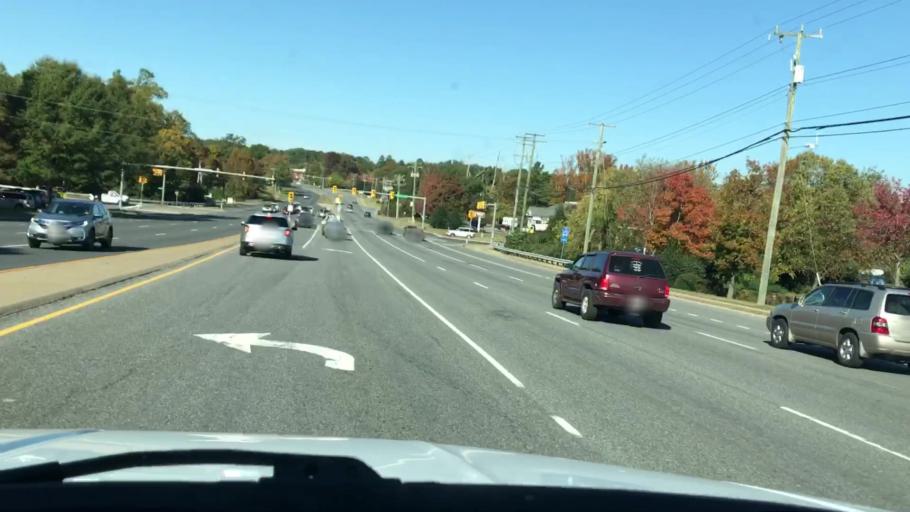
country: US
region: Virginia
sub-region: Henrico County
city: Short Pump
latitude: 37.6435
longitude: -77.5673
